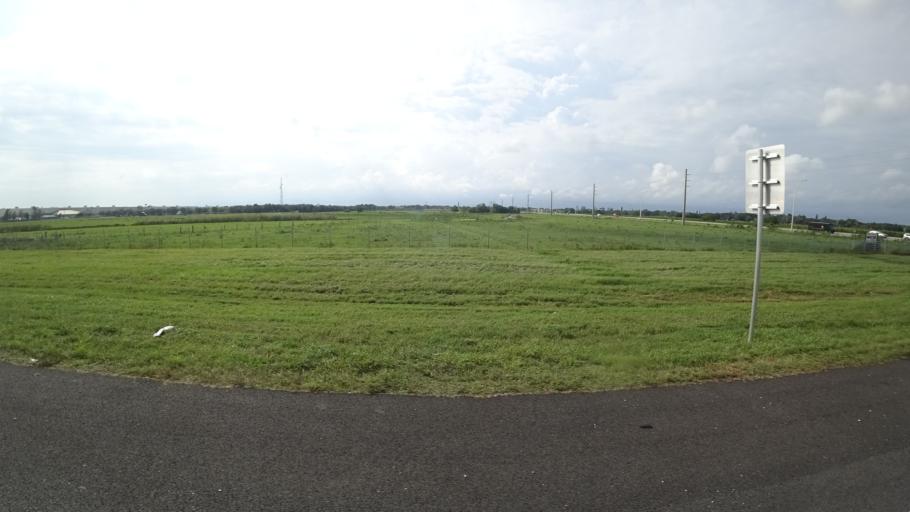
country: US
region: Florida
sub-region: Manatee County
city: Samoset
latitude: 27.4608
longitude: -82.5305
